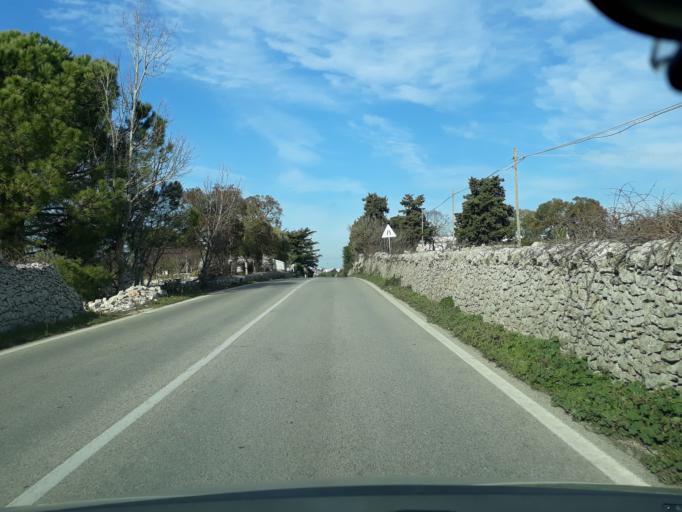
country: IT
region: Apulia
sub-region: Provincia di Taranto
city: Martina Franca
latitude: 40.7287
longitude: 17.3326
